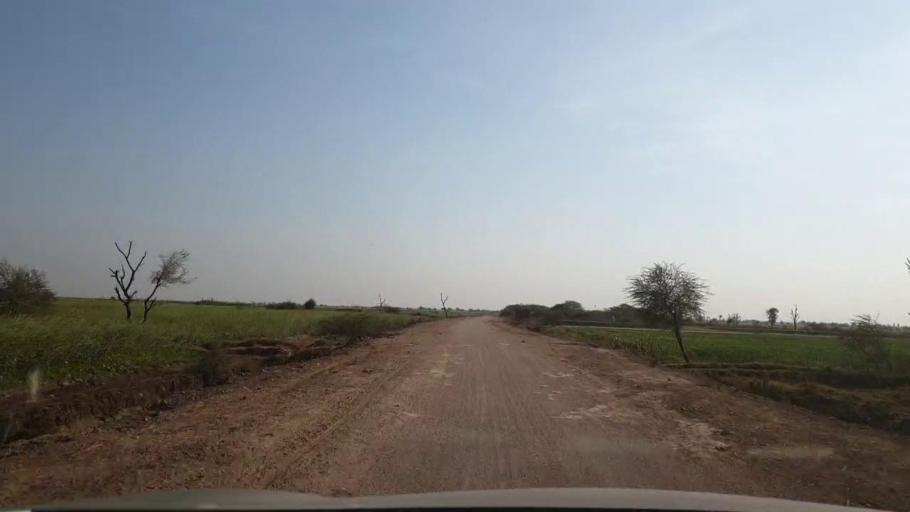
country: PK
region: Sindh
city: Berani
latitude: 25.7144
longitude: 68.8066
